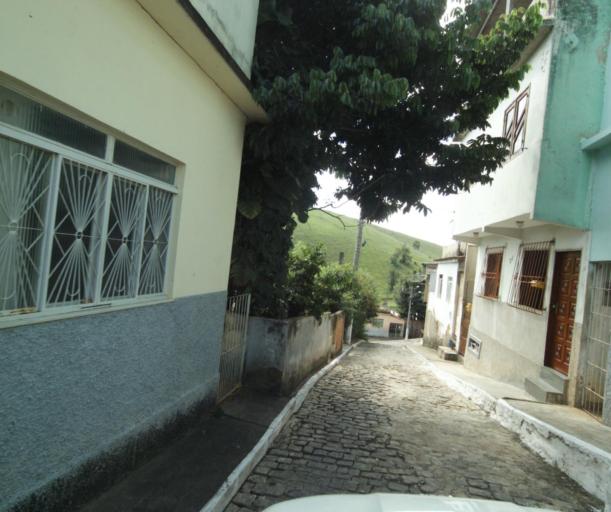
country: BR
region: Espirito Santo
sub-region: Sao Jose Do Calcado
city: Sao Jose do Calcado
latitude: -21.0252
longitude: -41.6570
